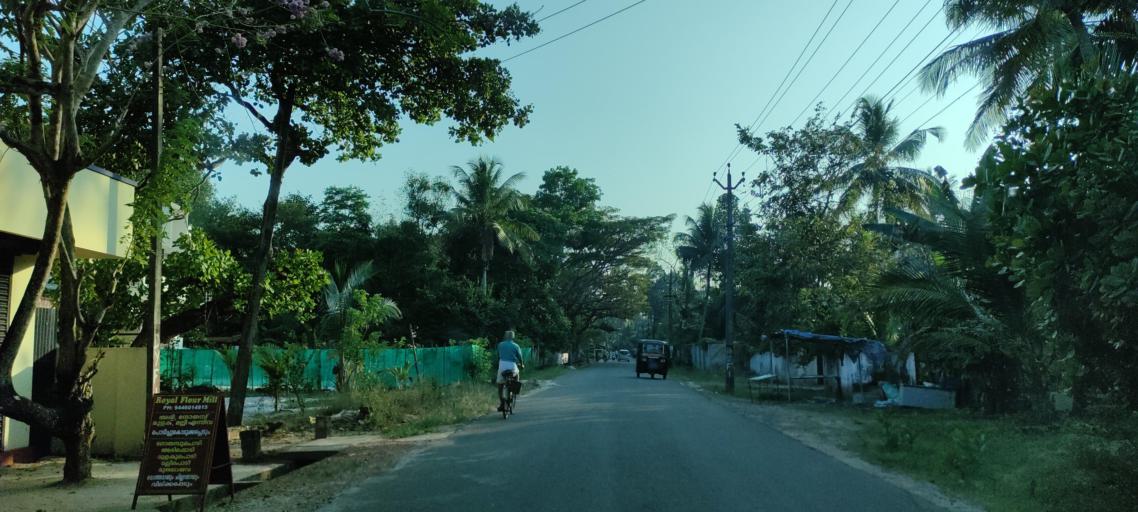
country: IN
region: Kerala
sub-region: Alappuzha
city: Shertallai
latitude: 9.6541
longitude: 76.3577
